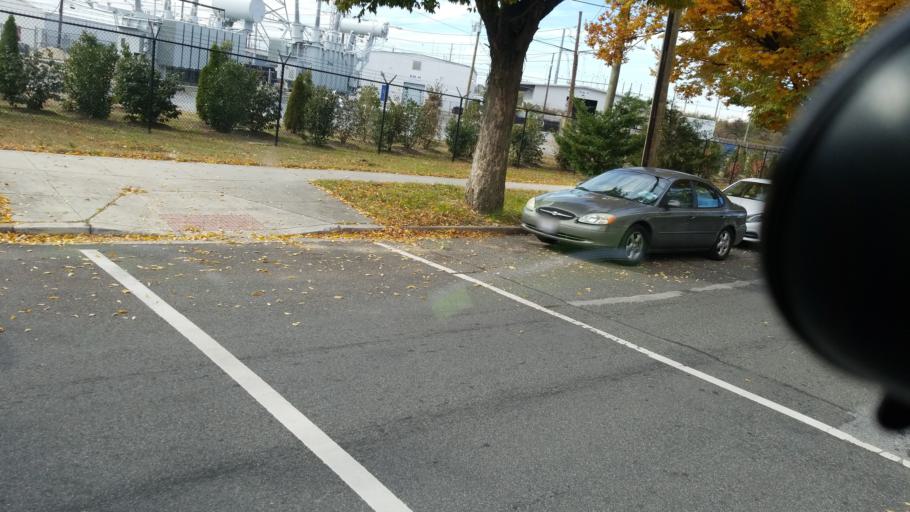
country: US
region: Maryland
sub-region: Prince George's County
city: Colmar Manor
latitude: 38.8997
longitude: -76.9525
